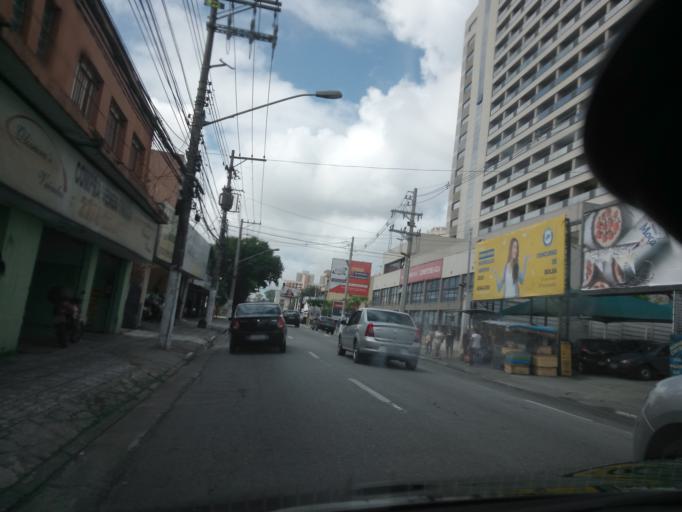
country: BR
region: Sao Paulo
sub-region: Sao Bernardo Do Campo
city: Sao Bernardo do Campo
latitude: -23.7088
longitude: -46.5533
